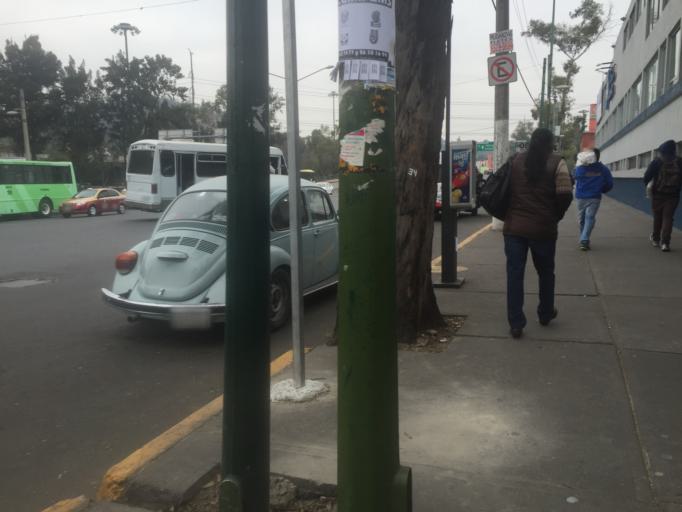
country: MX
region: Mexico
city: Colonia Lindavista
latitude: 19.4933
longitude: -99.1214
